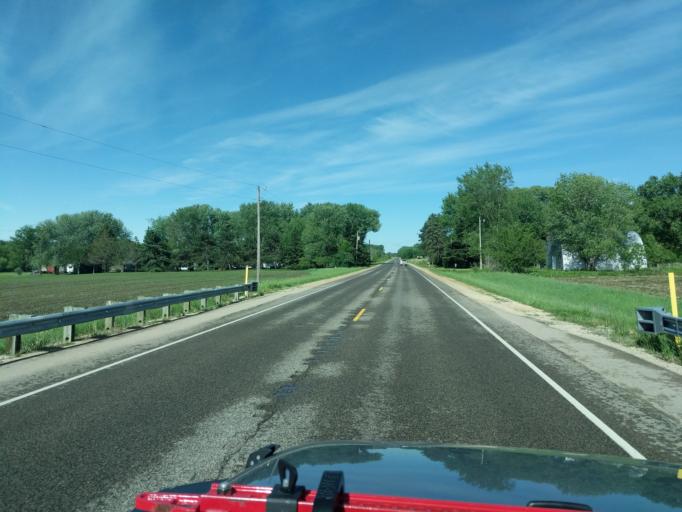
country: US
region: Wisconsin
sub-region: Pierce County
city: River Falls
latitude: 44.8508
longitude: -92.5857
